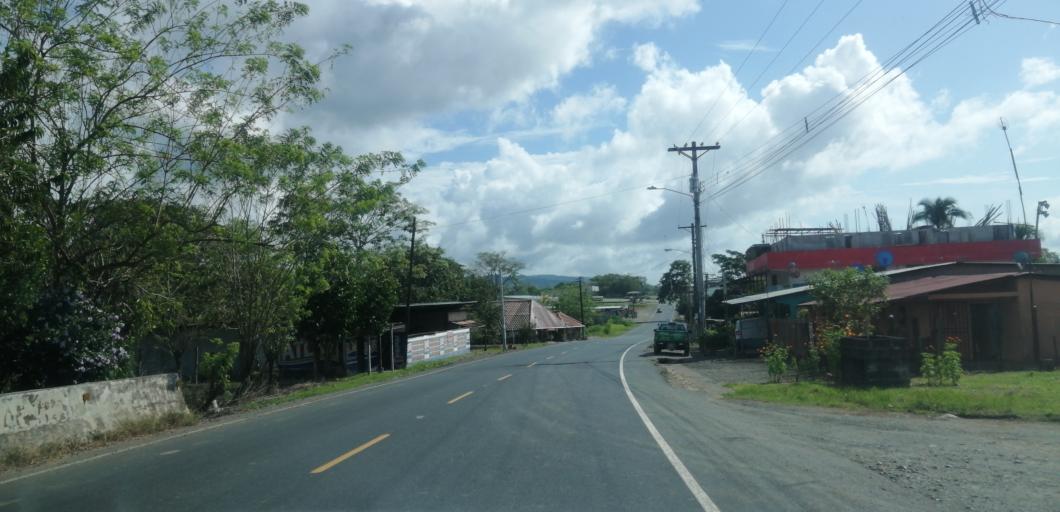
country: PA
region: Panama
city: Canita
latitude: 9.2214
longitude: -78.8966
